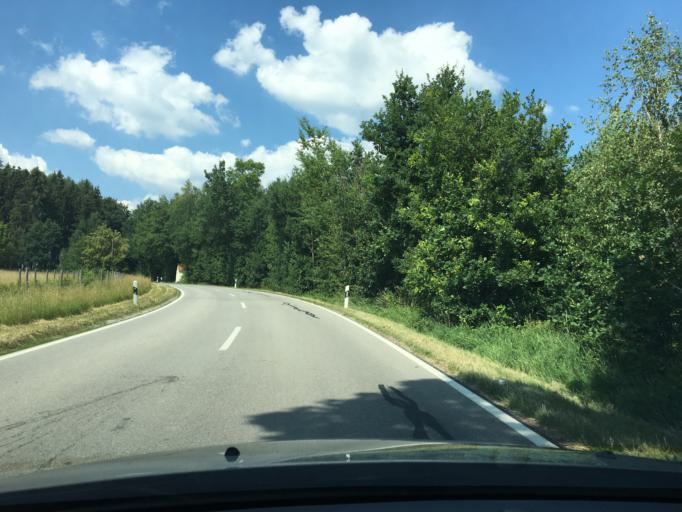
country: DE
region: Bavaria
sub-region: Upper Bavaria
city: Neumarkt-Sankt Veit
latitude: 48.3720
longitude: 12.5068
